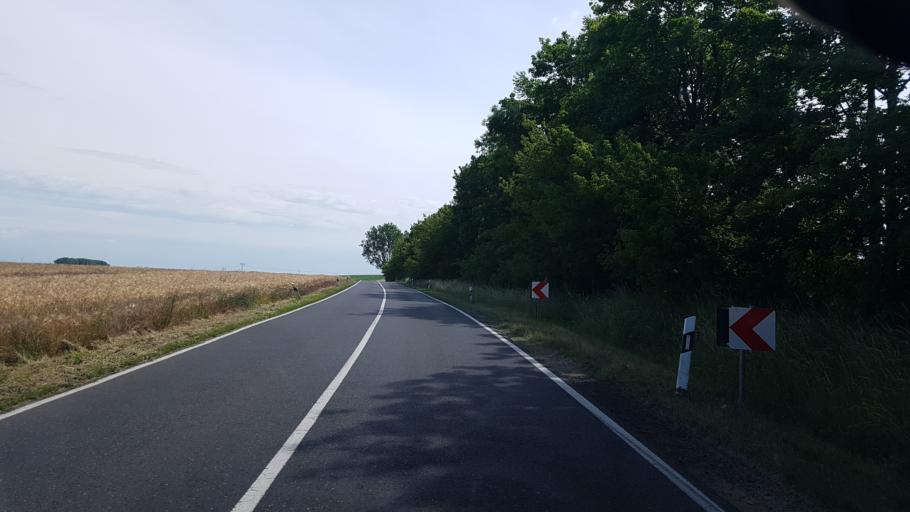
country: DE
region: Brandenburg
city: Prenzlau
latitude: 53.3490
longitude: 13.7919
